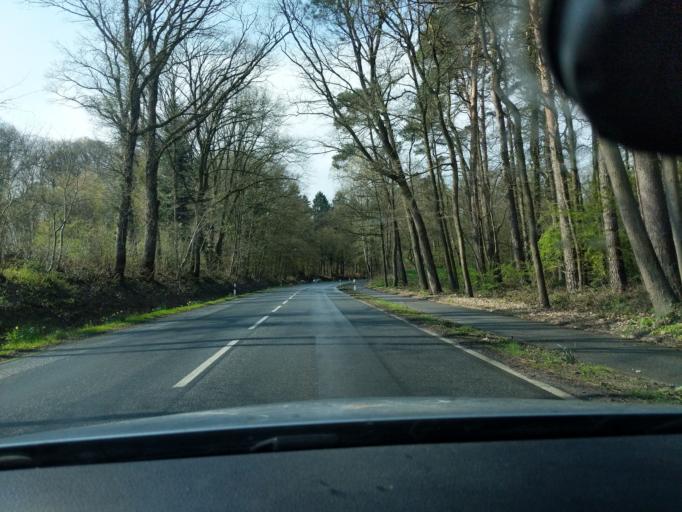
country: DE
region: Lower Saxony
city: Harsefeld
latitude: 53.4638
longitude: 9.5009
